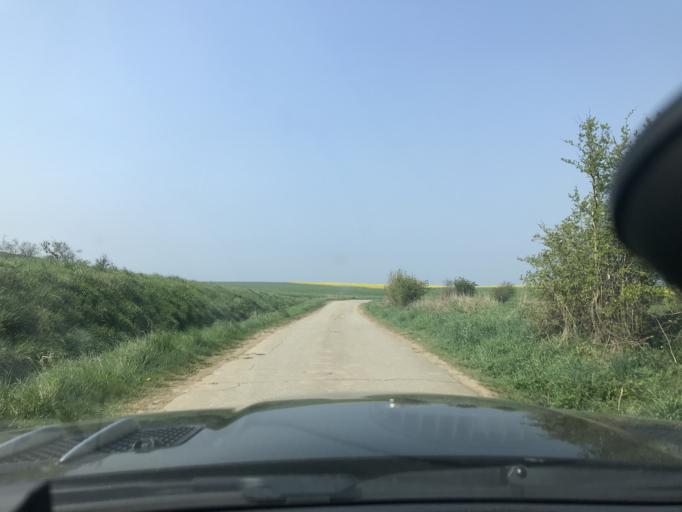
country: DE
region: Schleswig-Holstein
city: Gremersdorf
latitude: 54.3665
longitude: 10.9178
